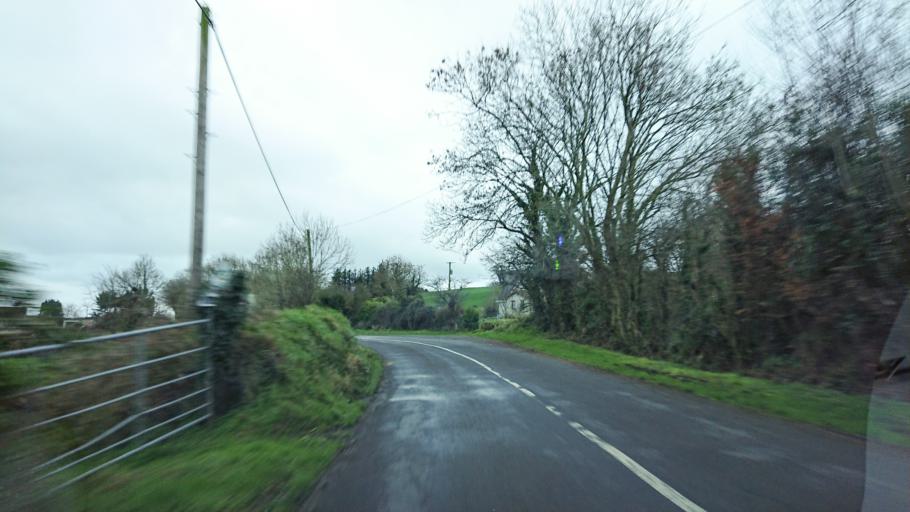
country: IE
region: Munster
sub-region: Waterford
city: Portlaw
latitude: 52.1689
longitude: -7.3928
